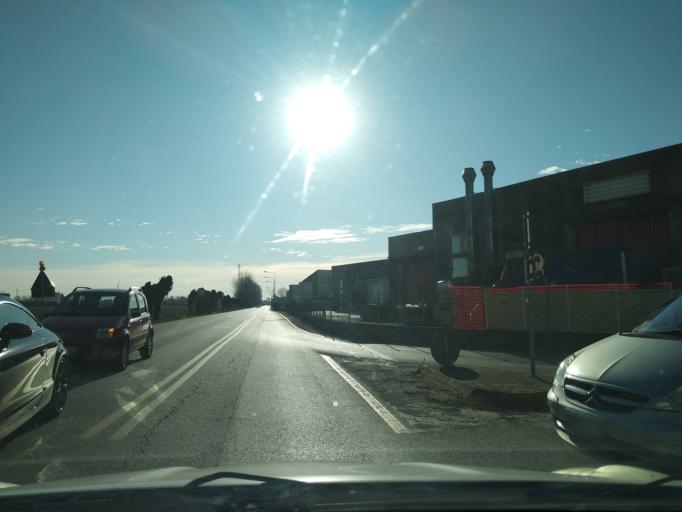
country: IT
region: Veneto
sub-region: Provincia di Vicenza
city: Quinto Vicentino
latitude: 45.5881
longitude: 11.6450
